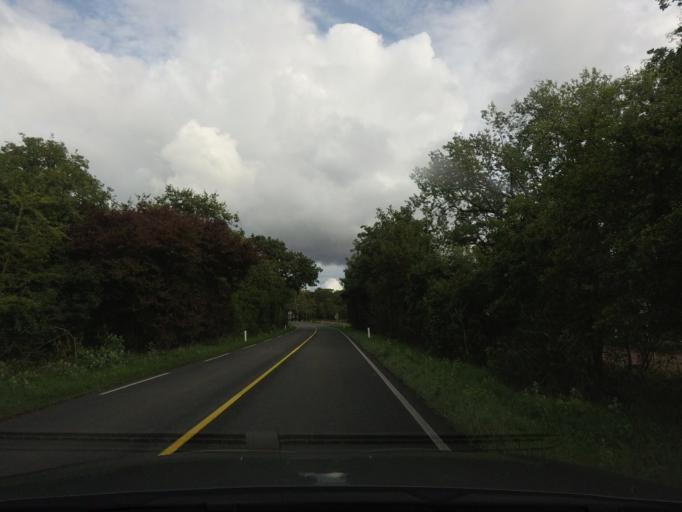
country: NL
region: North Holland
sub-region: Gemeente Bloemendaal
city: Bloemendaal
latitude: 52.3963
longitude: 4.5868
